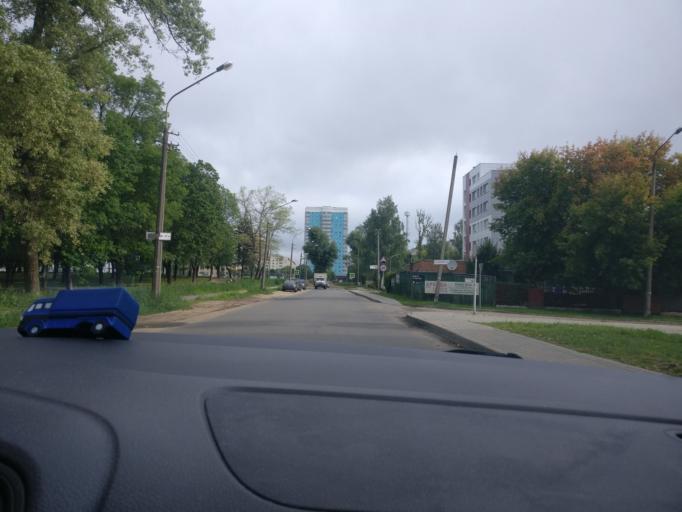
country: BY
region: Minsk
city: Minsk
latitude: 53.8731
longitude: 27.5550
